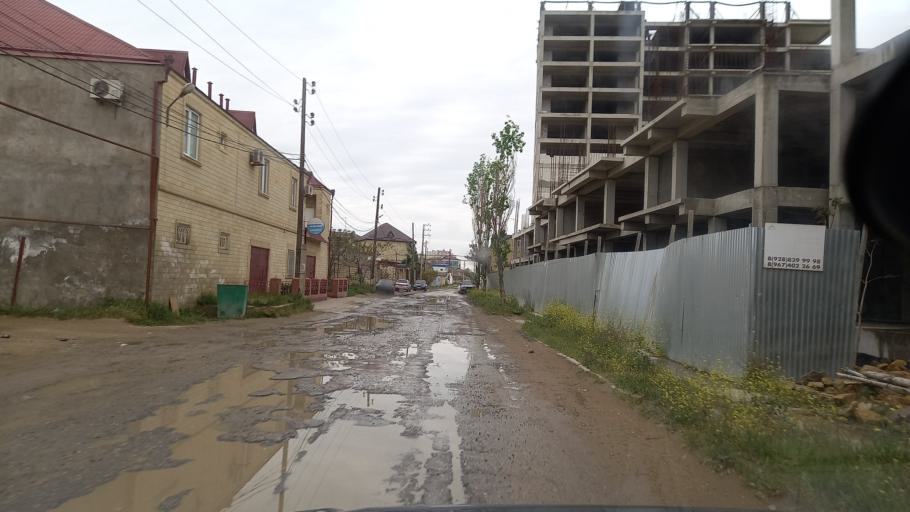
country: RU
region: Dagestan
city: Derbent
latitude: 42.0691
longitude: 48.3010
